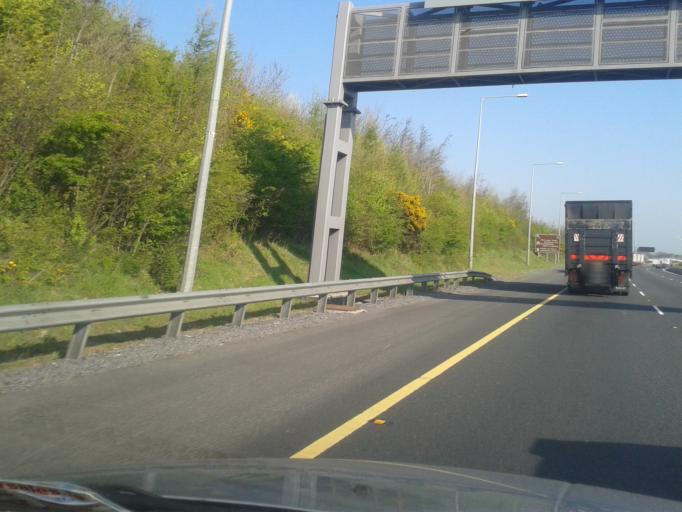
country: IE
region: Leinster
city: Kinsealy-Drinan
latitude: 53.4562
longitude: -6.2034
